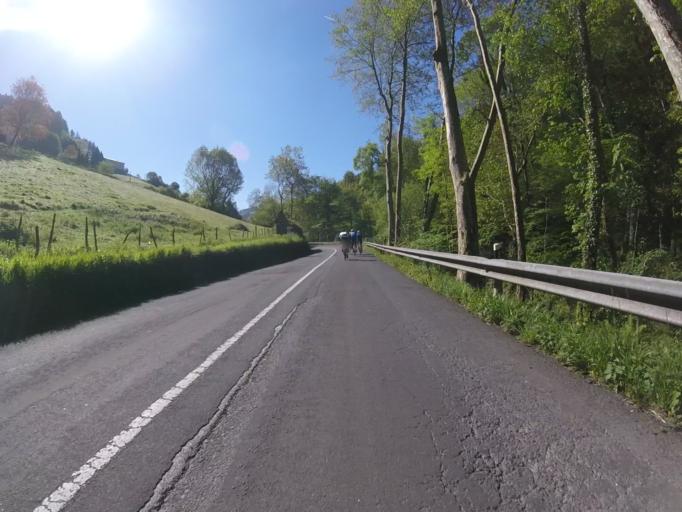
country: ES
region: Basque Country
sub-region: Provincia de Guipuzcoa
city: Errezil
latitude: 43.1736
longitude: -2.2004
